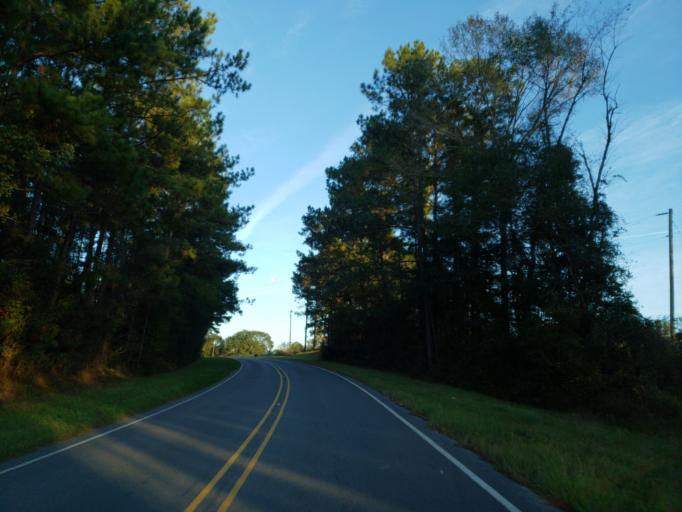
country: US
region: Mississippi
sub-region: Wayne County
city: Belmont
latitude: 31.4412
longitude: -88.5088
